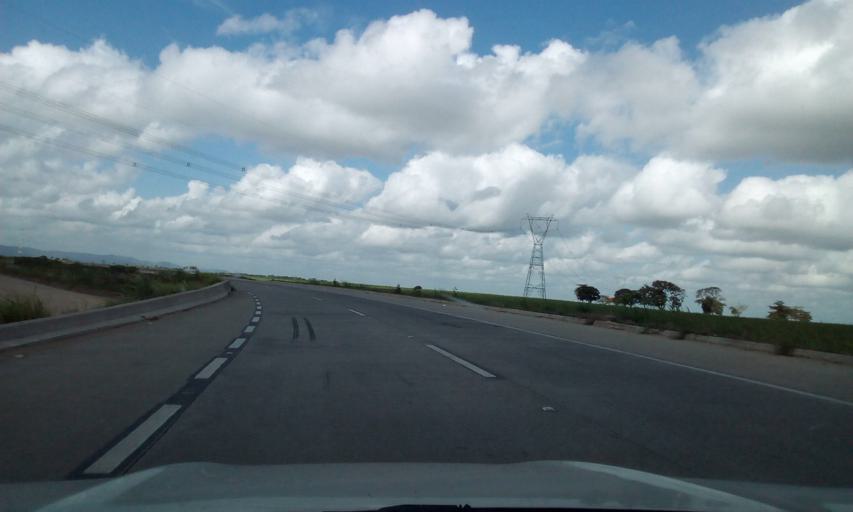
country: BR
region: Alagoas
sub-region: Messias
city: Messias
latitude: -9.4016
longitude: -35.8372
